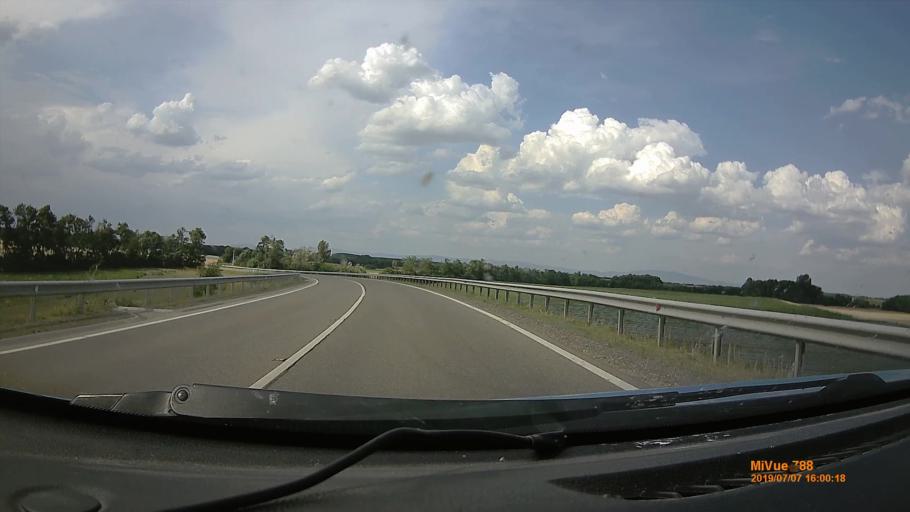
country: HU
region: Heves
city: Boldog
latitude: 47.5974
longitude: 19.7498
